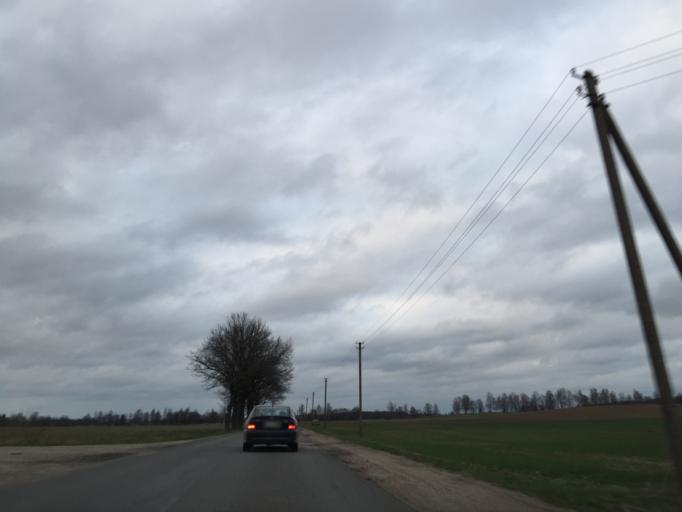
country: LT
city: Skaudvile
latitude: 55.4864
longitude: 22.5859
